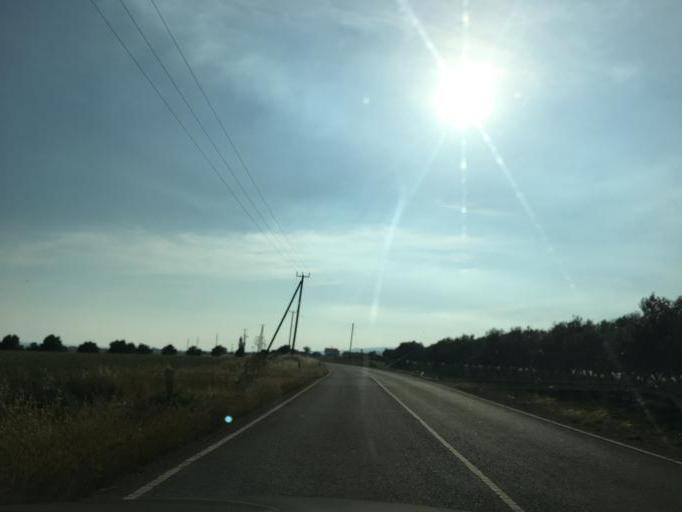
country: CY
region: Larnaka
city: Kofinou
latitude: 34.7831
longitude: 33.4761
